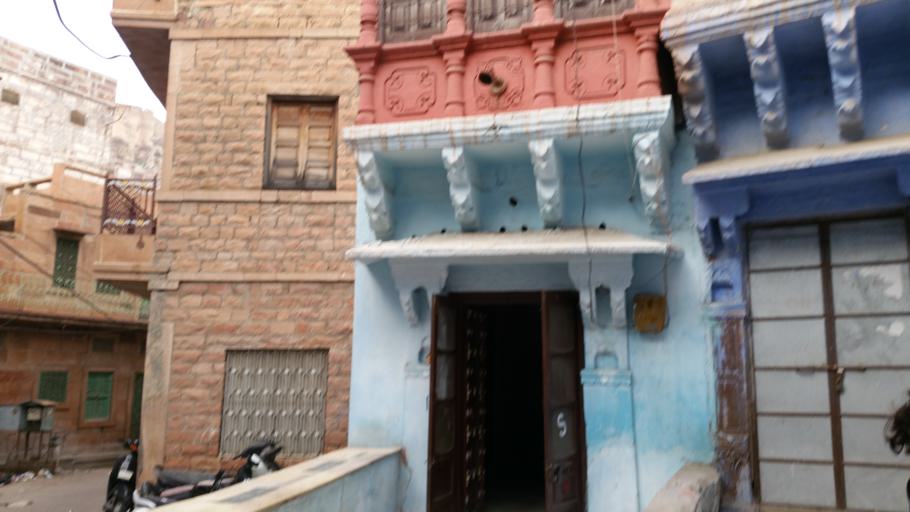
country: IN
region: Rajasthan
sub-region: Jodhpur
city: Jodhpur
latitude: 26.2949
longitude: 73.0194
